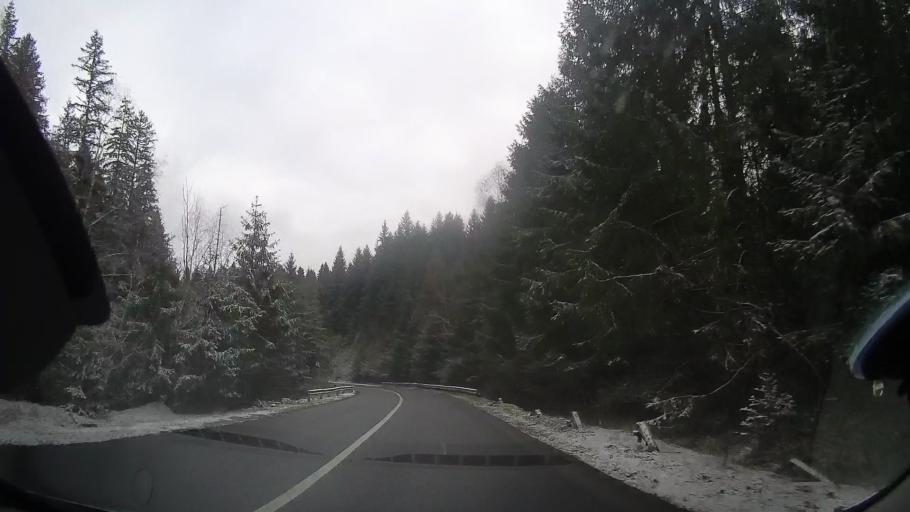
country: RO
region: Cluj
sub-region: Comuna Calatele
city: Calatele
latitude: 46.7299
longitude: 23.0327
